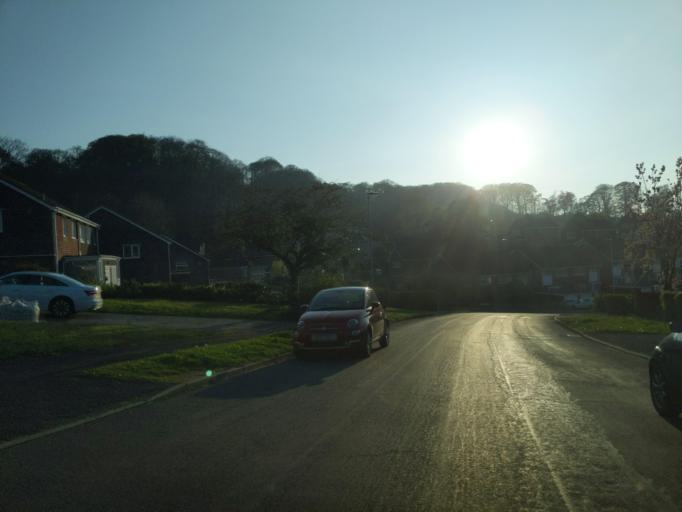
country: GB
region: England
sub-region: Plymouth
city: Plymstock
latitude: 50.3489
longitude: -4.0881
